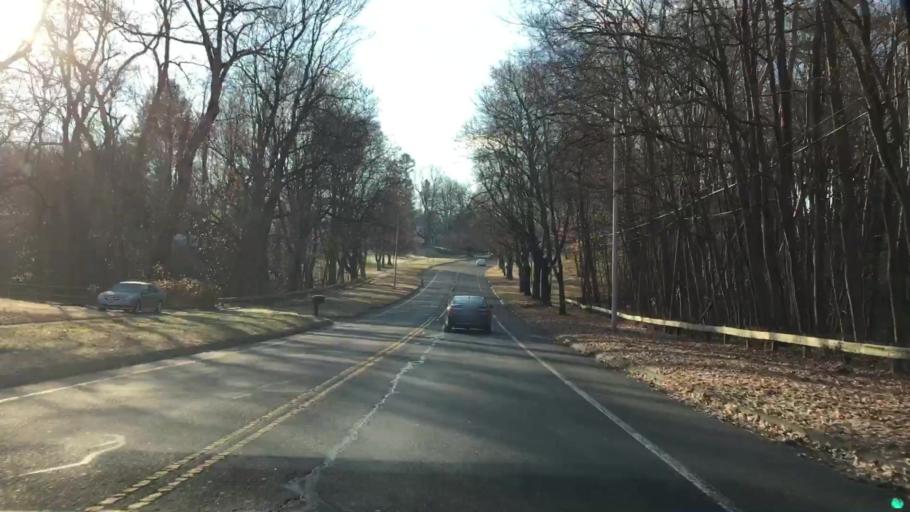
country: US
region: Massachusetts
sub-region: Hampden County
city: Longmeadow
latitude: 42.0309
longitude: -72.5818
